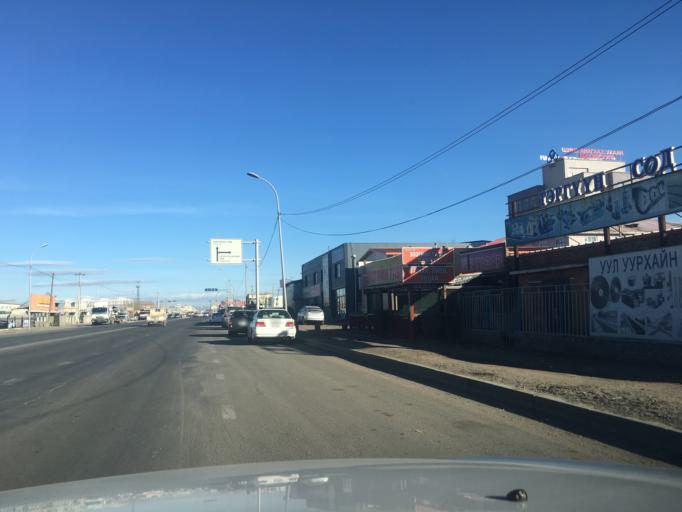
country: MN
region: Ulaanbaatar
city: Ulaanbaatar
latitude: 47.9070
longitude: 106.7823
